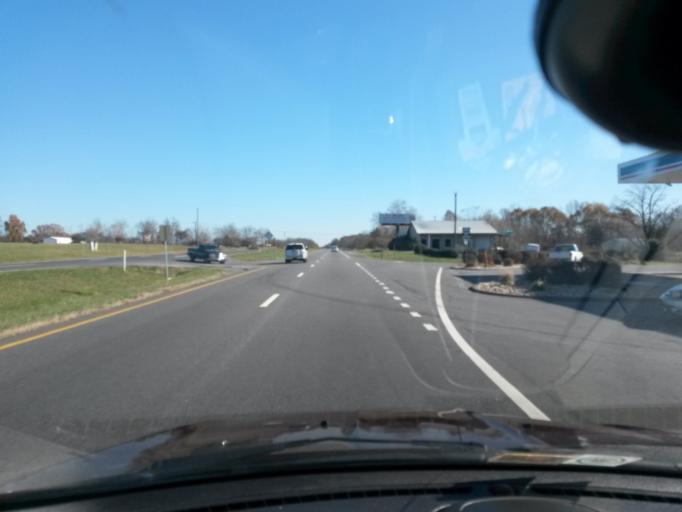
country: US
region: Virginia
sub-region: Bedford County
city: Forest
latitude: 37.3006
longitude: -79.3532
